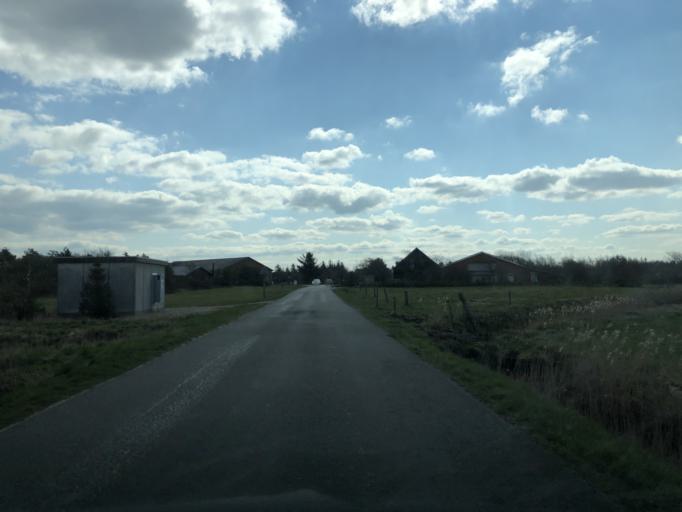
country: DK
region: Central Jutland
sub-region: Holstebro Kommune
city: Ulfborg
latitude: 56.3962
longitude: 8.2232
